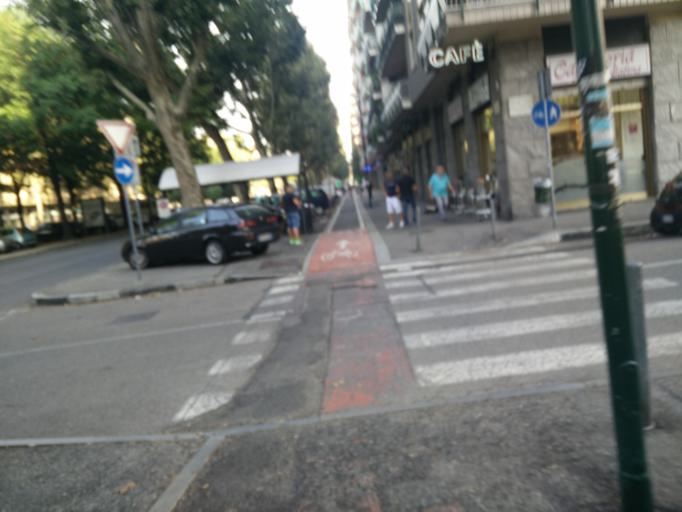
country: IT
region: Piedmont
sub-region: Provincia di Torino
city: Nichelino
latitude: 45.0227
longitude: 7.6488
